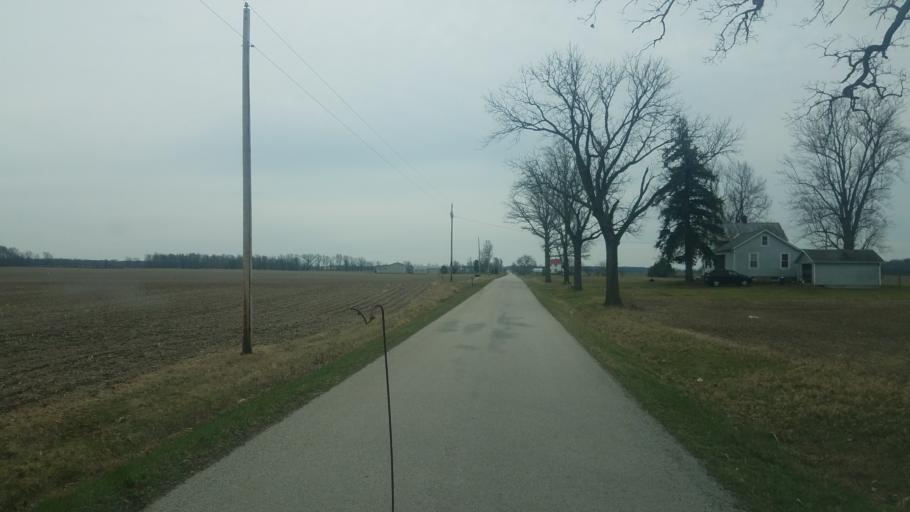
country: US
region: Ohio
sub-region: Huron County
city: Greenwich
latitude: 41.1311
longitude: -82.5646
